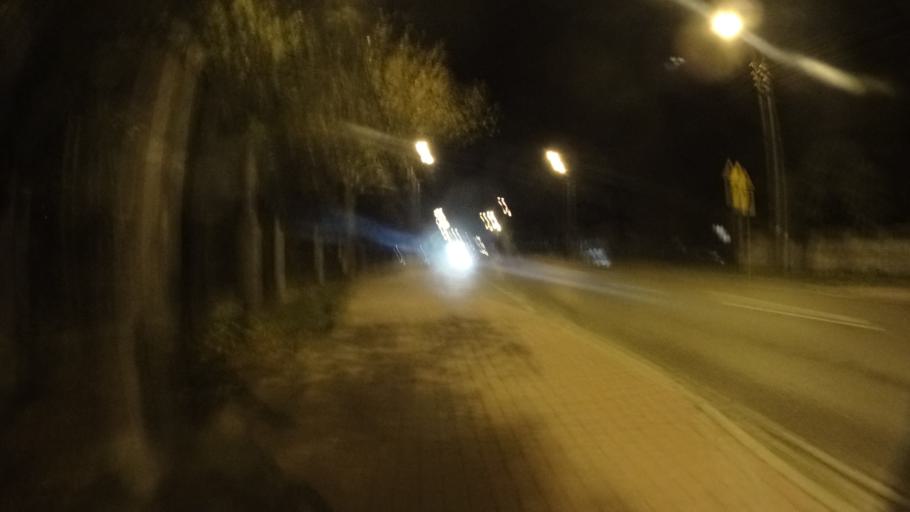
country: PL
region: Masovian Voivodeship
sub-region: Powiat warszawski zachodni
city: Hornowek
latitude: 52.2540
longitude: 20.7969
